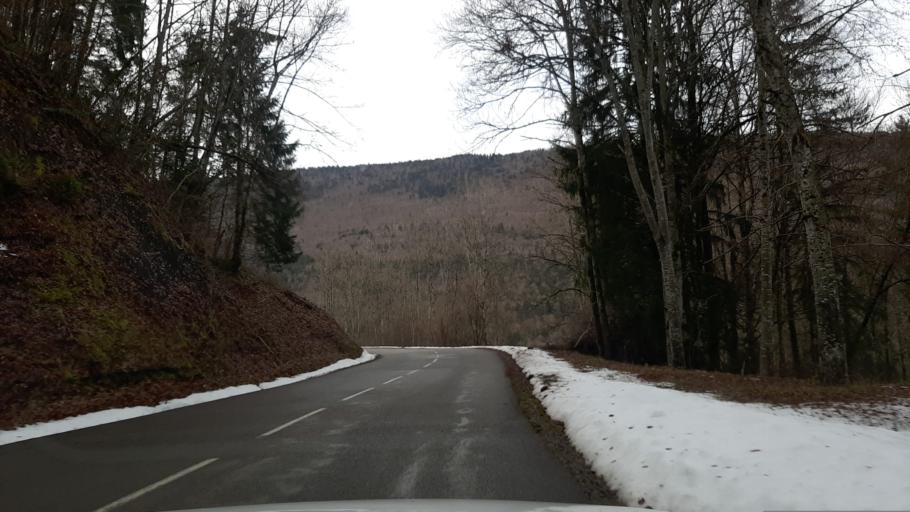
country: FR
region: Rhone-Alpes
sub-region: Departement de la Haute-Savoie
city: Cusy
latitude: 45.6672
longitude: 6.1025
